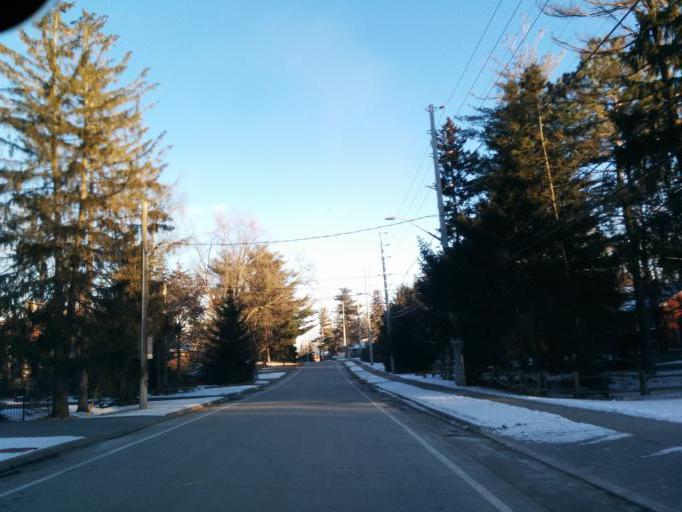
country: CA
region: Ontario
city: Mississauga
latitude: 43.5480
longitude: -79.6101
